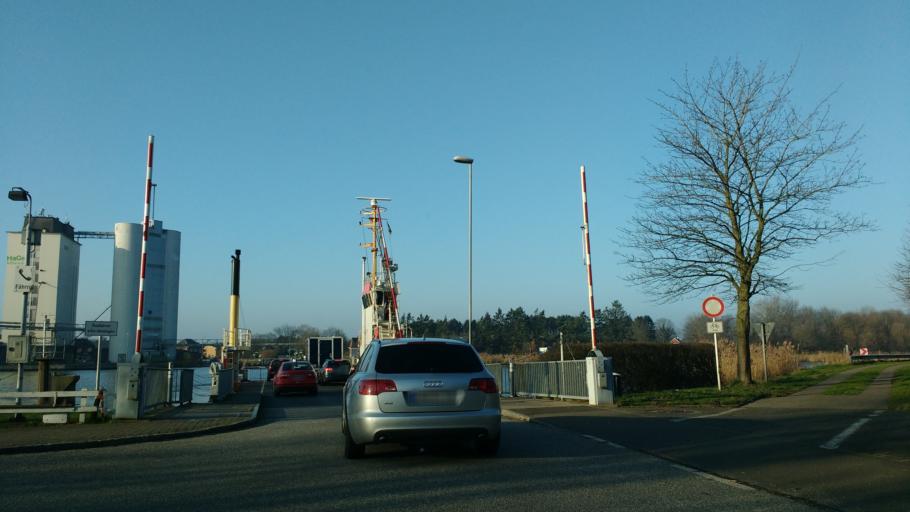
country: DE
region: Schleswig-Holstein
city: Hochdonn
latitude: 54.0187
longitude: 9.3002
